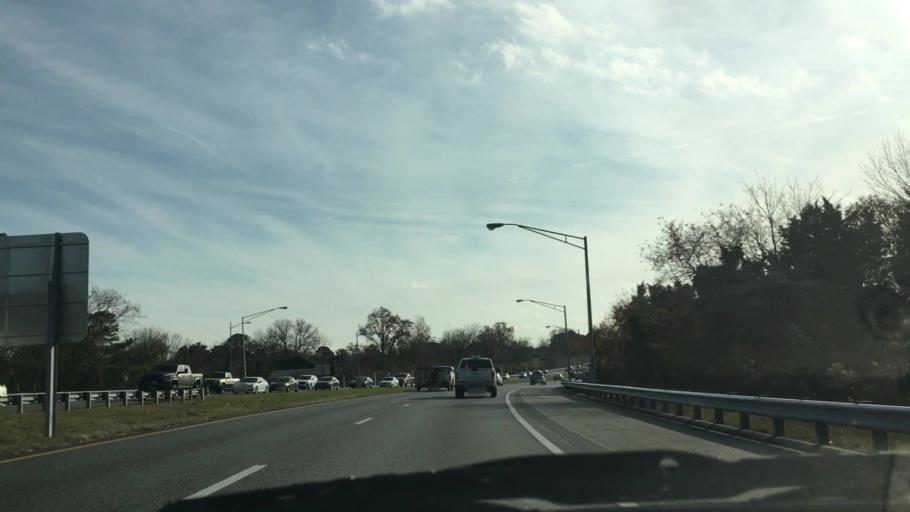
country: US
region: Virginia
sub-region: City of Hampton
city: East Hampton
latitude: 36.9567
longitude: -76.2643
